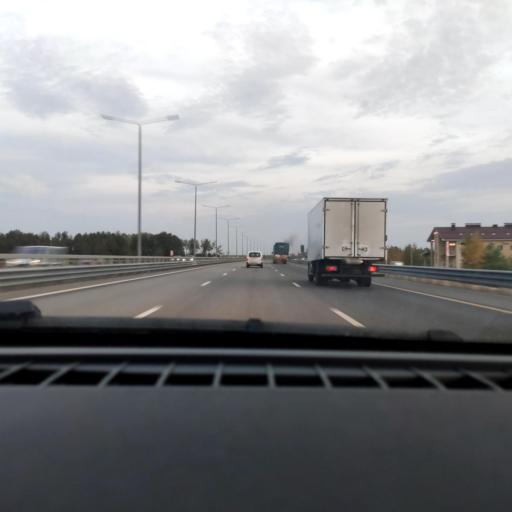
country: RU
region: Voronezj
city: Somovo
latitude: 51.7815
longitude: 39.2934
